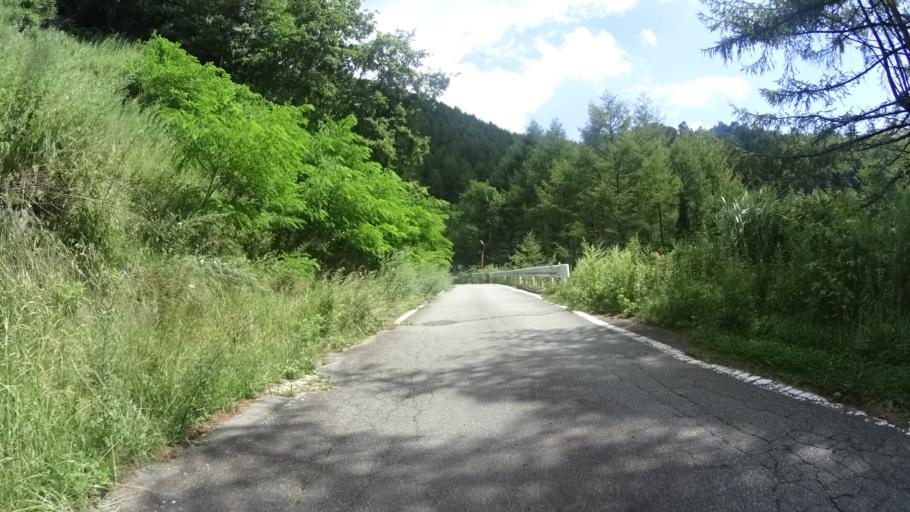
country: JP
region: Yamanashi
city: Enzan
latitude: 35.8346
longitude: 138.6407
